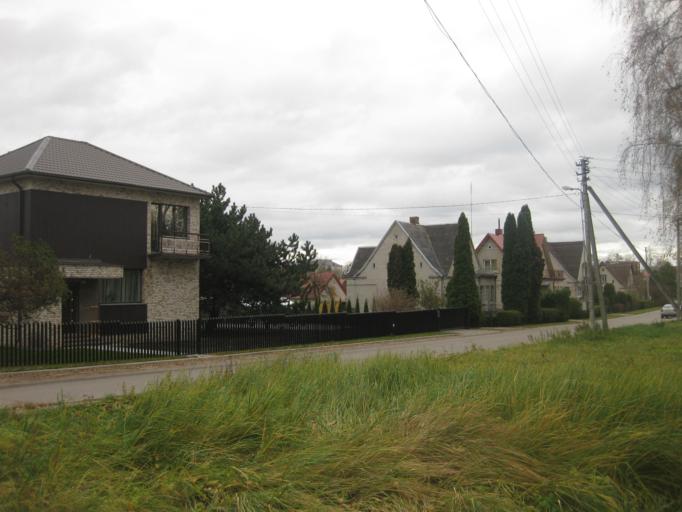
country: LT
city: Prienai
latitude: 54.6412
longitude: 23.9433
